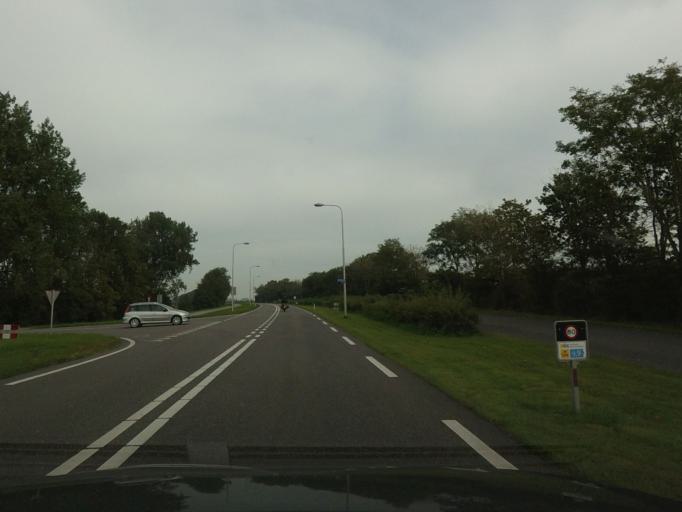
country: NL
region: North Holland
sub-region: Gemeente Schagen
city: Schagen
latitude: 52.8676
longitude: 4.8481
